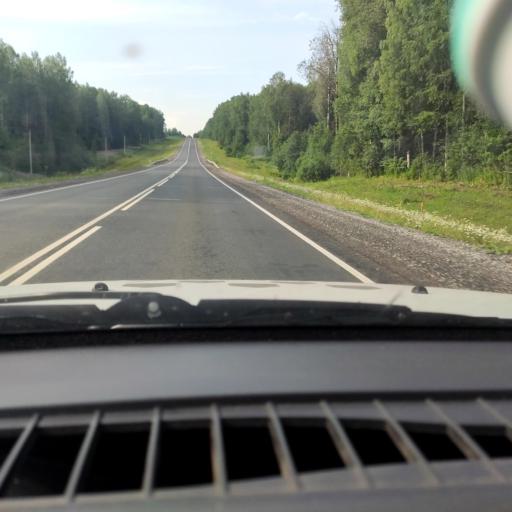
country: RU
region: Perm
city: Siva
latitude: 58.6139
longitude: 53.8700
